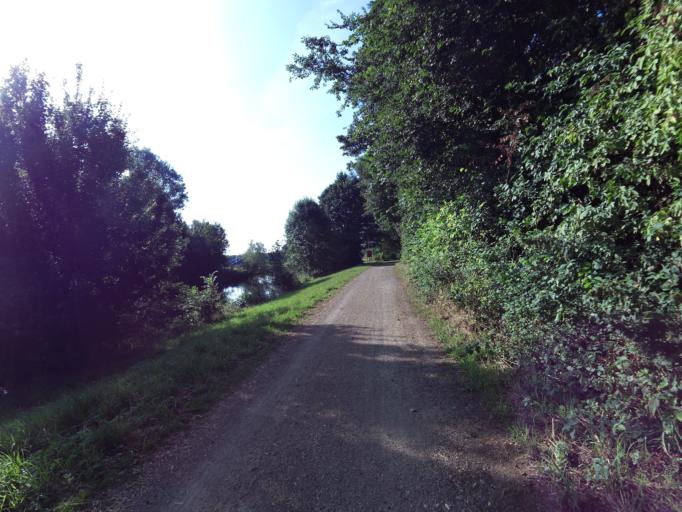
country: DE
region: North Rhine-Westphalia
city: Huckelhoven
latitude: 51.0316
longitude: 6.2337
